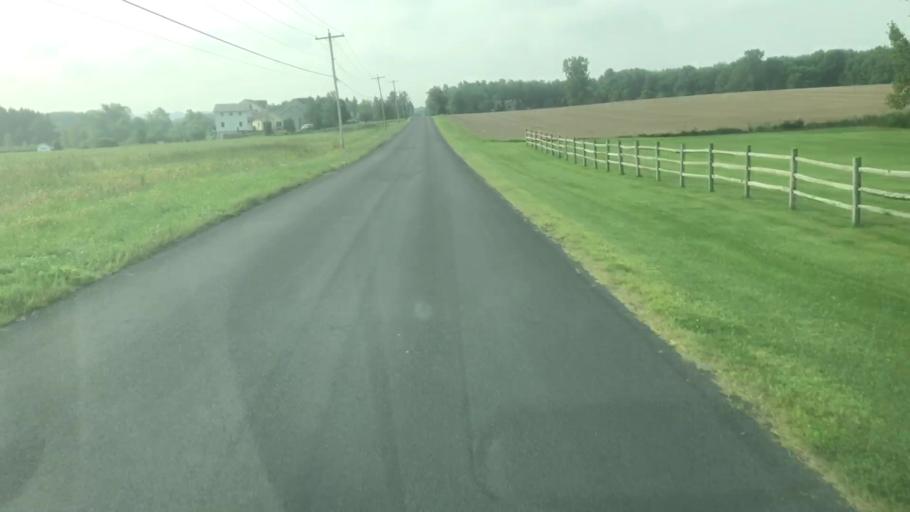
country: US
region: New York
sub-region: Onondaga County
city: Skaneateles
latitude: 42.9263
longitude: -76.4572
